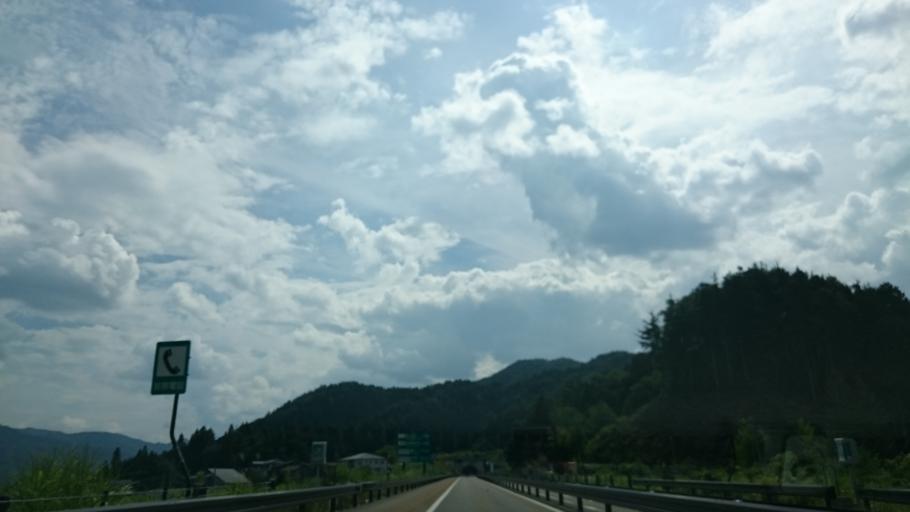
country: JP
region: Gifu
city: Takayama
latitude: 36.1634
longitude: 137.2258
